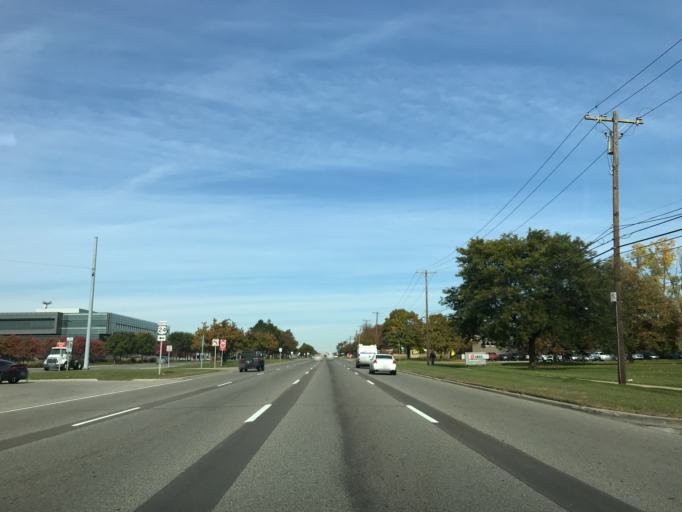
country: US
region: Michigan
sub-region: Oakland County
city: Southfield
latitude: 42.4504
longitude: -83.2780
